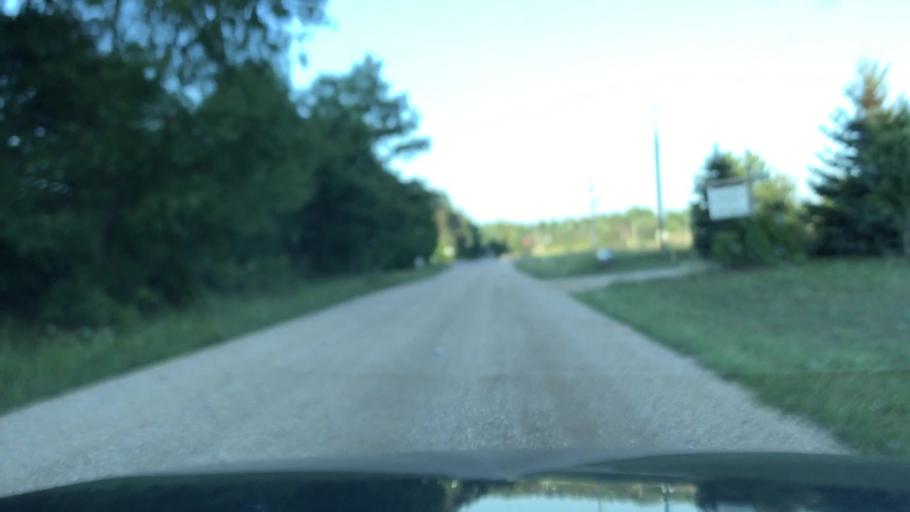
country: US
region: Michigan
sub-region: Osceola County
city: Evart
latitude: 43.8649
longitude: -85.3562
